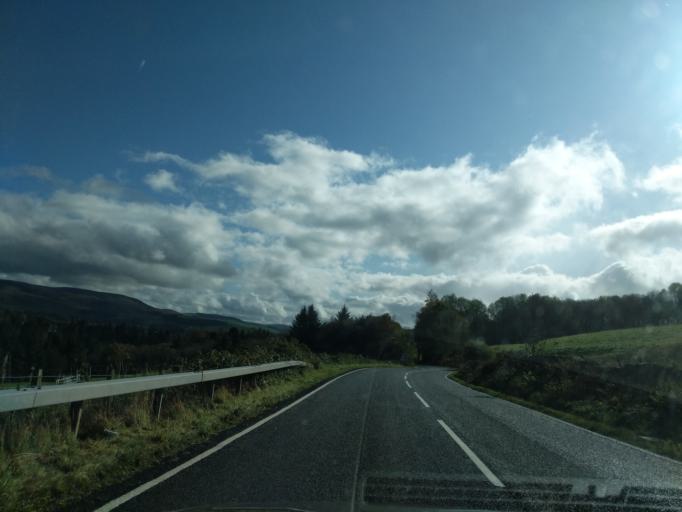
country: GB
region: Scotland
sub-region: Dumfries and Galloway
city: Moffat
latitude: 55.3434
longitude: -3.4597
